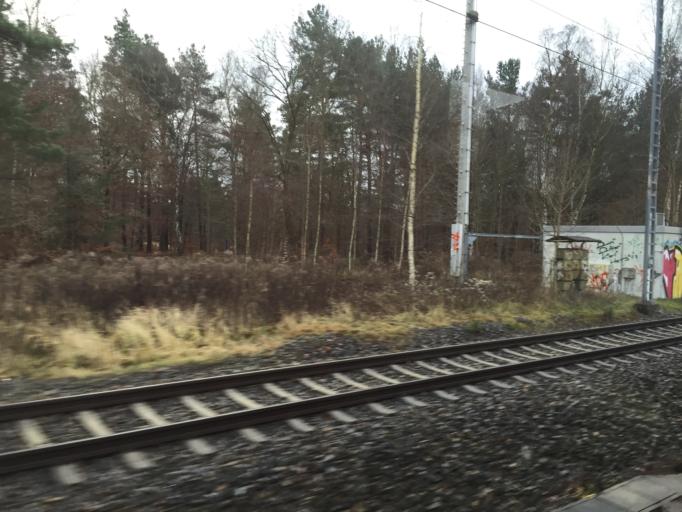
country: DE
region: Saxony
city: Albertstadt
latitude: 51.1161
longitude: 13.7905
